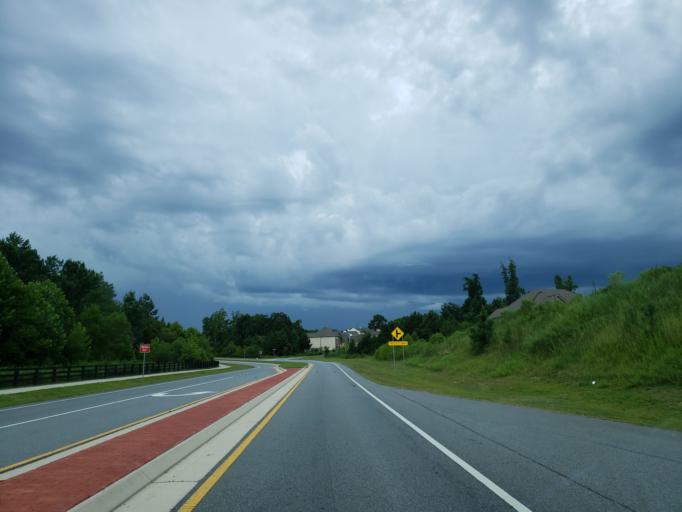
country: US
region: Georgia
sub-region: Bartow County
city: Emerson
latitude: 34.0307
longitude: -84.7713
